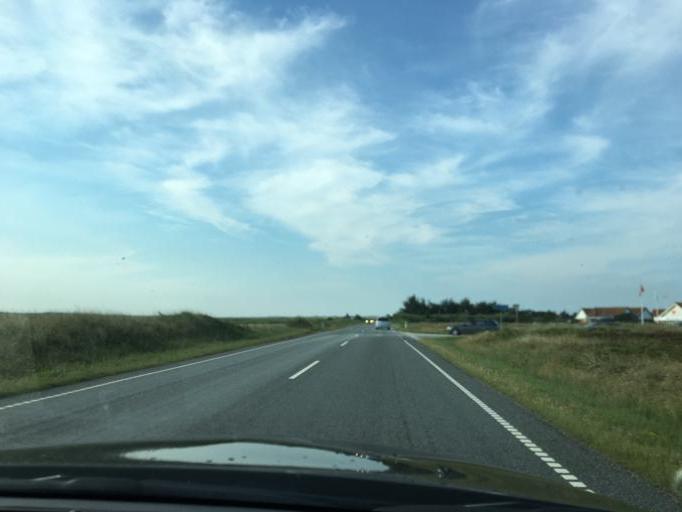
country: DK
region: Central Jutland
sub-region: Ringkobing-Skjern Kommune
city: Hvide Sande
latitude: 55.8511
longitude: 8.1765
